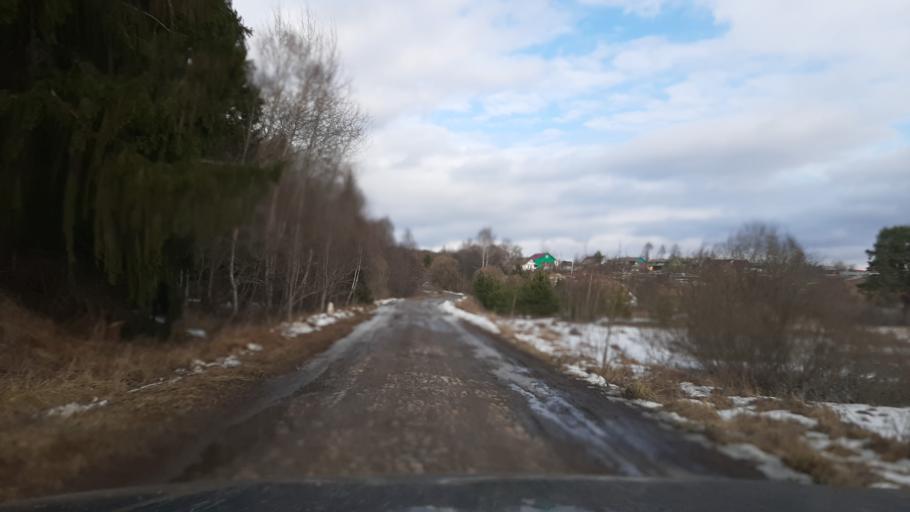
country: RU
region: Ivanovo
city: Teykovo
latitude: 56.8969
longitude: 40.6730
